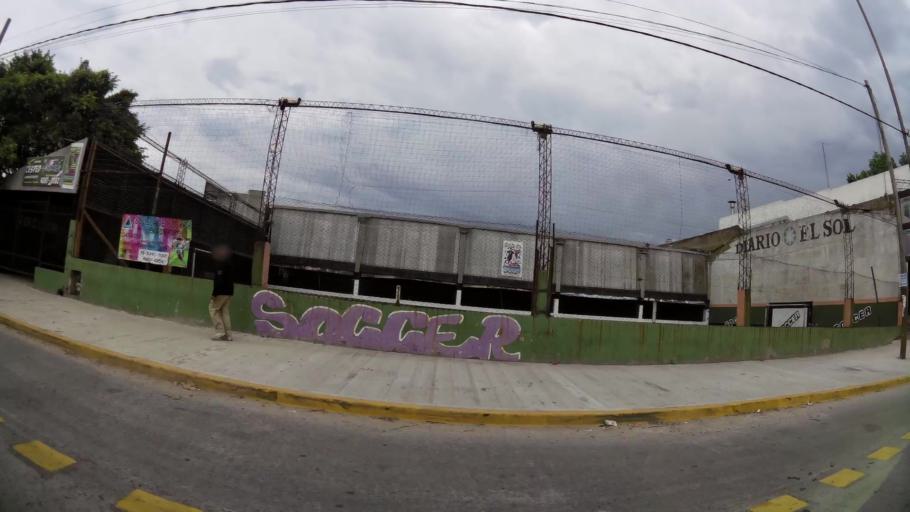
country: AR
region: Buenos Aires
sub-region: Partido de Quilmes
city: Quilmes
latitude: -34.7455
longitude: -58.2880
